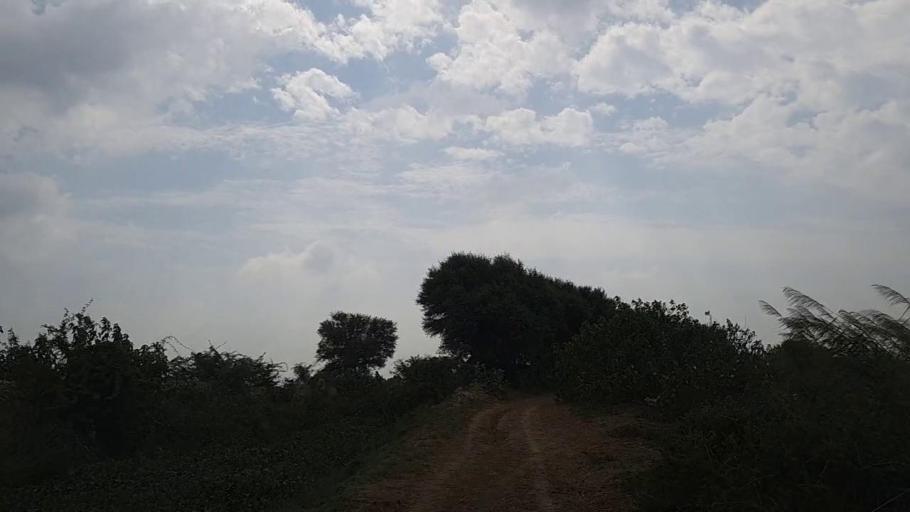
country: PK
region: Sindh
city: Mirpur Batoro
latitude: 24.6155
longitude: 68.1358
